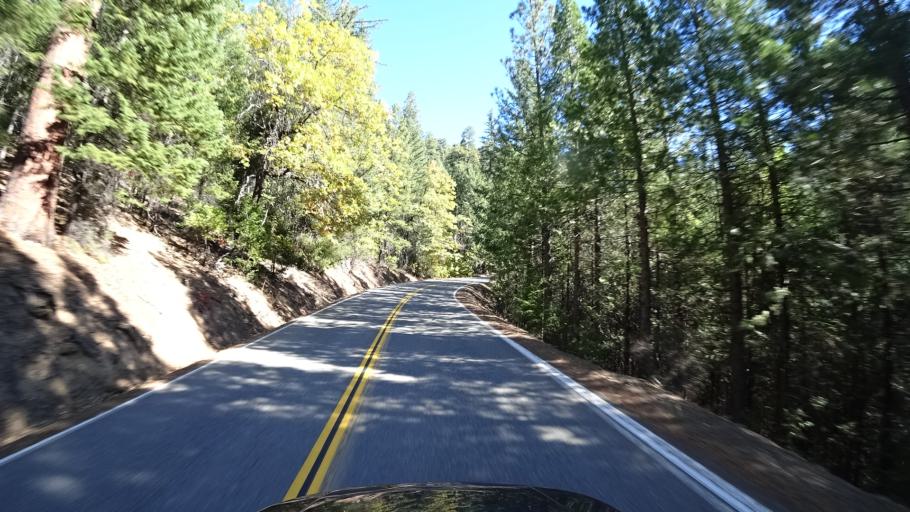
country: US
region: California
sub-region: Trinity County
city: Weaverville
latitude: 41.2121
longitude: -123.0362
